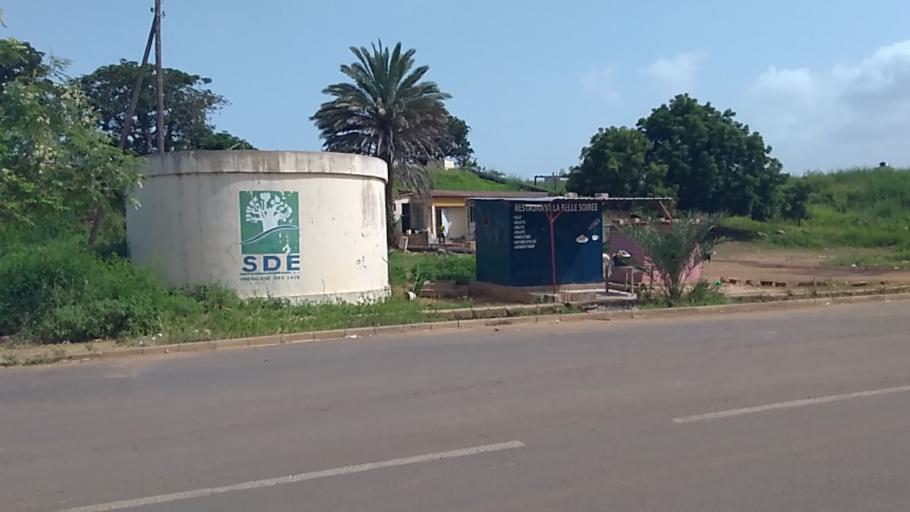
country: SN
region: Dakar
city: Mermoz Boabab
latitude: 14.7231
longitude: -17.4966
